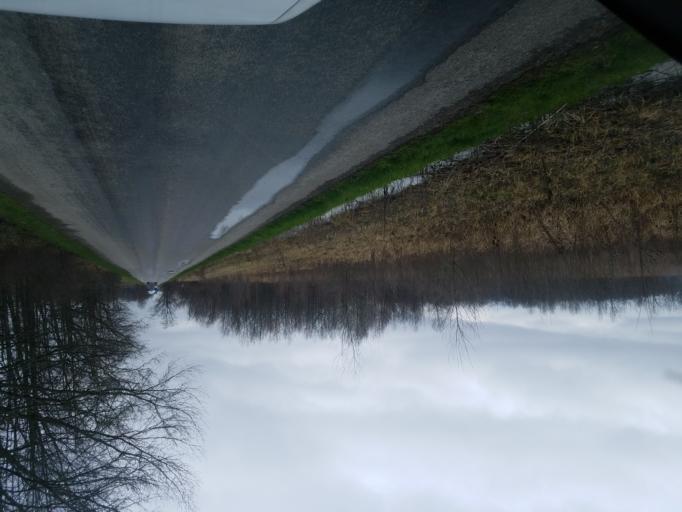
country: US
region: Ohio
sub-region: Wyandot County
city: Upper Sandusky
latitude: 40.6873
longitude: -83.3661
